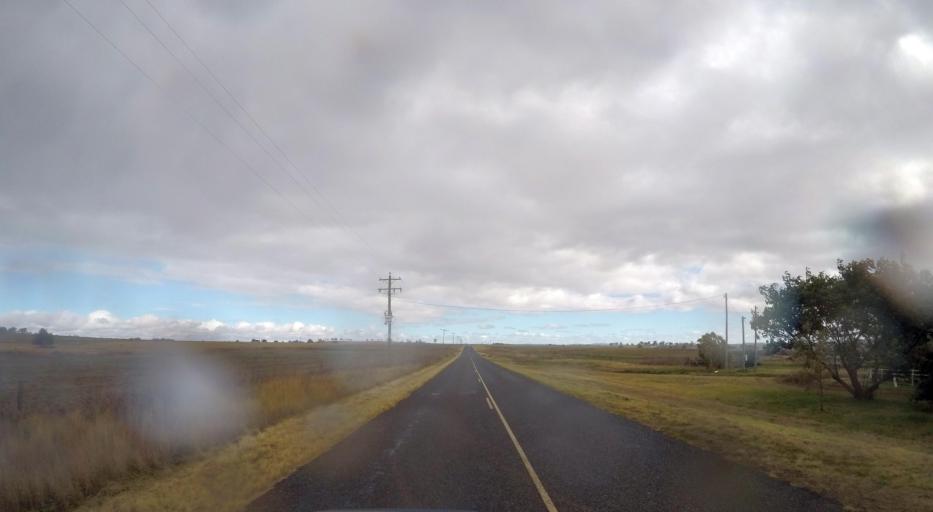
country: AU
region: Queensland
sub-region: Southern Downs
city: Warwick
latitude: -28.0519
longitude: 152.0321
